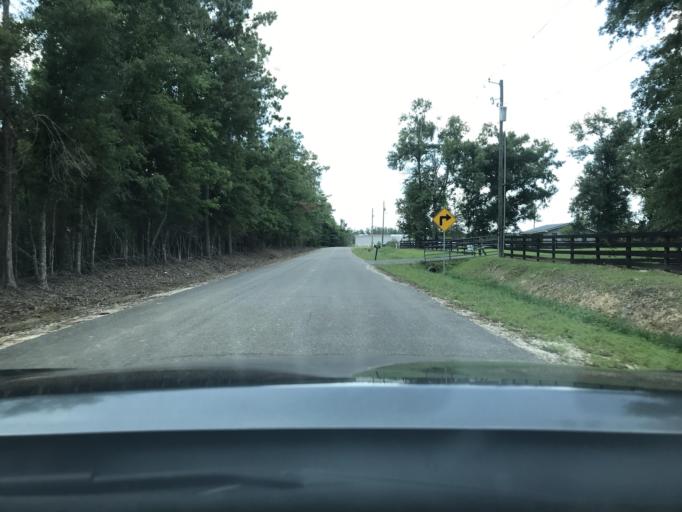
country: US
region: Louisiana
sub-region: Calcasieu Parish
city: Moss Bluff
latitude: 30.3342
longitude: -93.1308
